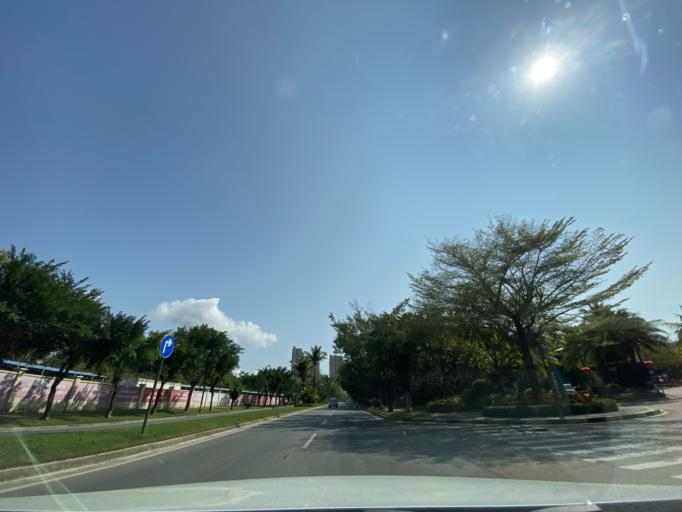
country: CN
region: Hainan
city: Yingzhou
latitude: 18.4173
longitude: 109.8854
